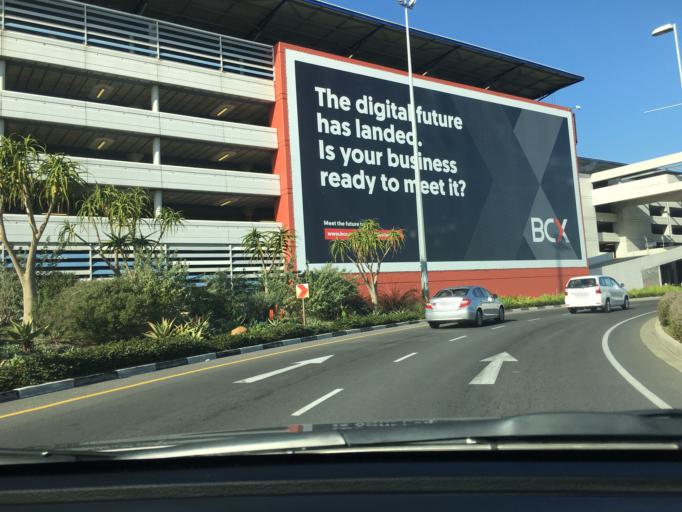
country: ZA
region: Western Cape
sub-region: City of Cape Town
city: Lansdowne
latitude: -33.9657
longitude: 18.5939
